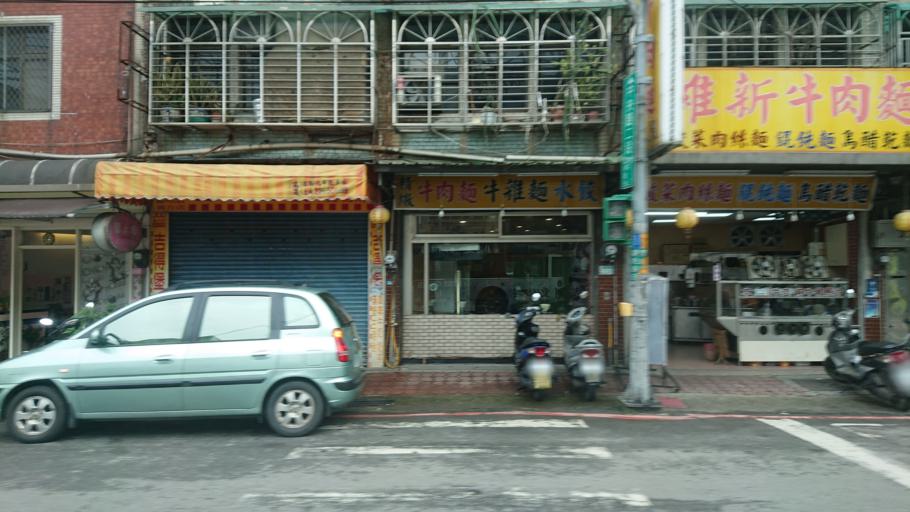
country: TW
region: Taipei
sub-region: Taipei
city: Banqiao
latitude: 24.9723
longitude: 121.4403
